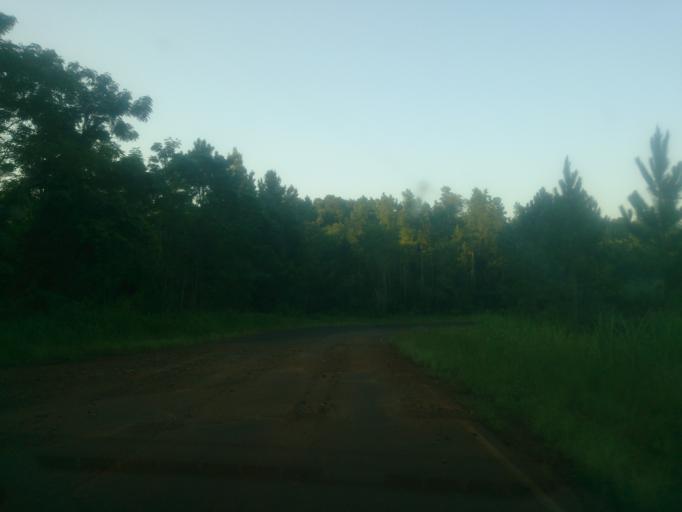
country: AR
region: Misiones
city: Panambi
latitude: -27.6654
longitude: -54.9150
